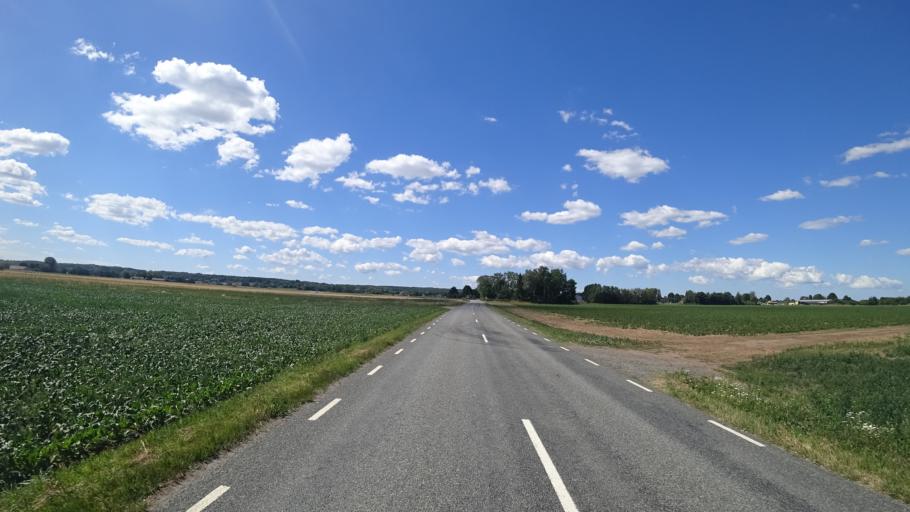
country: SE
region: Skane
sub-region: Kristianstads Kommun
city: Onnestad
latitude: 56.0604
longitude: 14.0394
